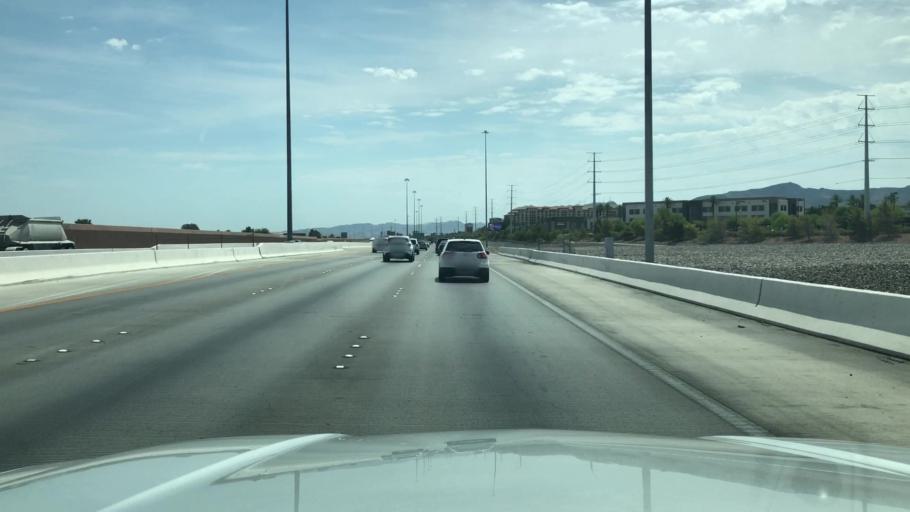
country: US
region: Nevada
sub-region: Clark County
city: Whitney
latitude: 36.0234
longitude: -115.1009
